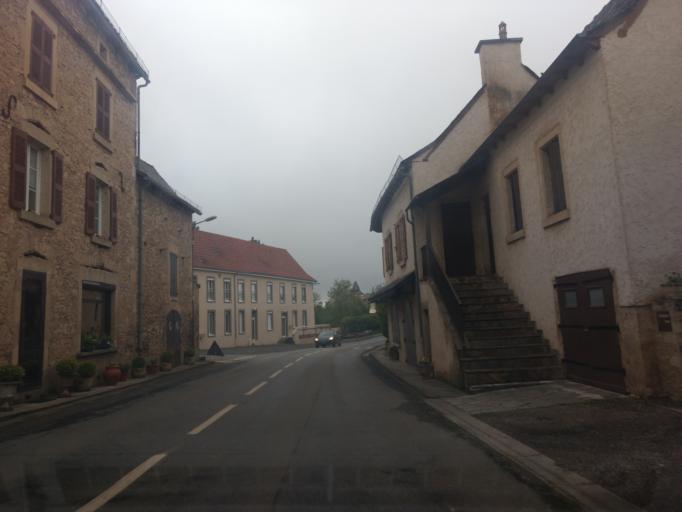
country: FR
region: Midi-Pyrenees
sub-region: Departement de l'Aveyron
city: Montbazens
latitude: 44.4542
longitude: 2.2525
